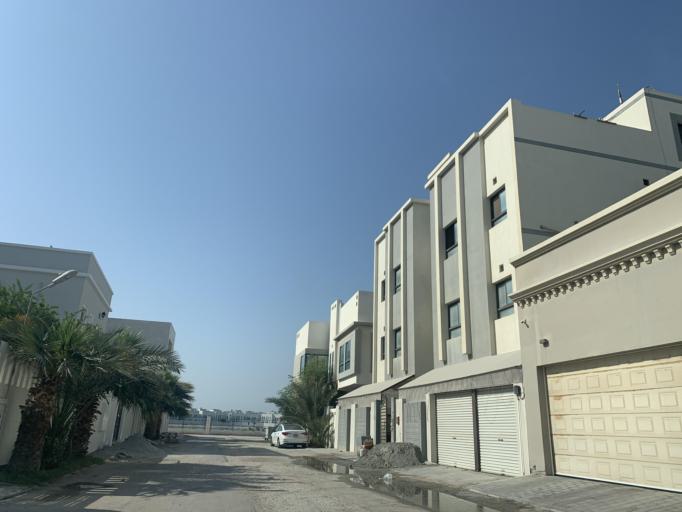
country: BH
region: Central Governorate
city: Madinat Hamad
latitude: 26.1324
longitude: 50.4873
